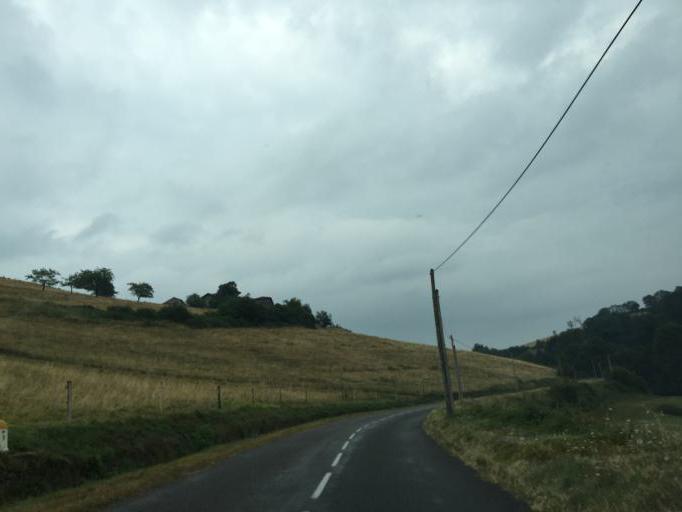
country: FR
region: Rhone-Alpes
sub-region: Departement de la Loire
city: Saint-Christo-en-Jarez
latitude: 45.5302
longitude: 4.4691
